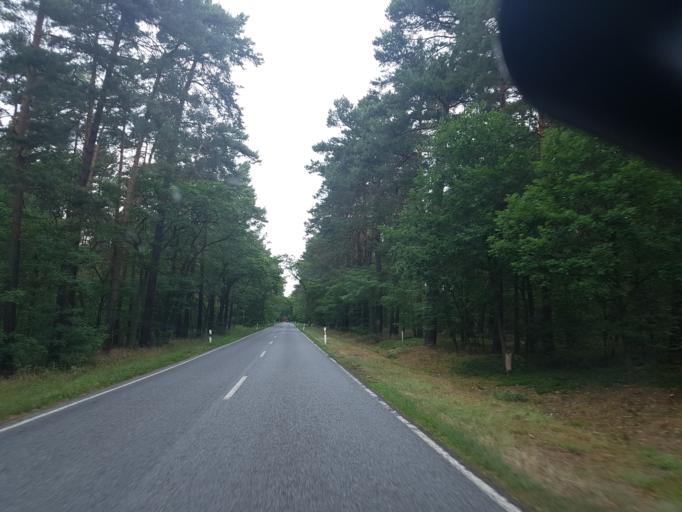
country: DE
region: Brandenburg
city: Lebusa
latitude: 51.8317
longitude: 13.4153
